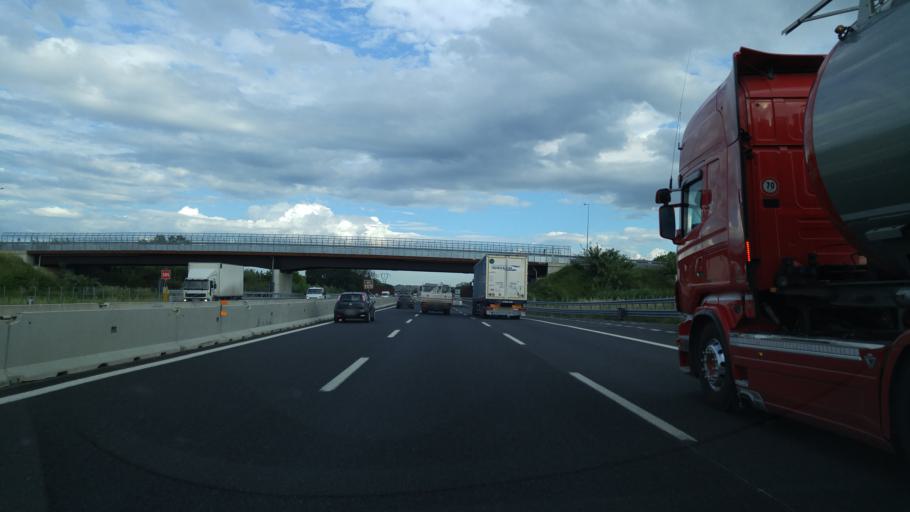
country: IT
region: Emilia-Romagna
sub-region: Provincia di Rimini
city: Coriano
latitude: 44.0000
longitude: 12.6083
